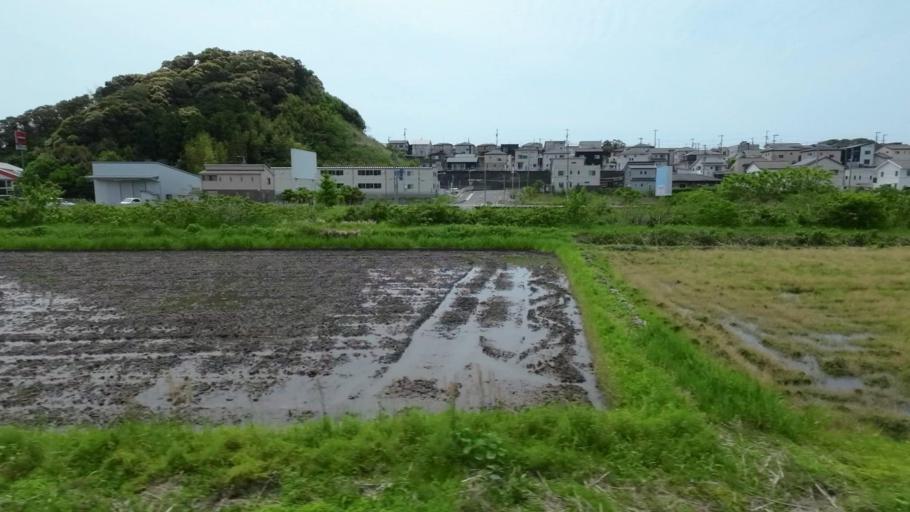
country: JP
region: Kochi
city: Kochi-shi
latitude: 33.5782
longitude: 133.6172
